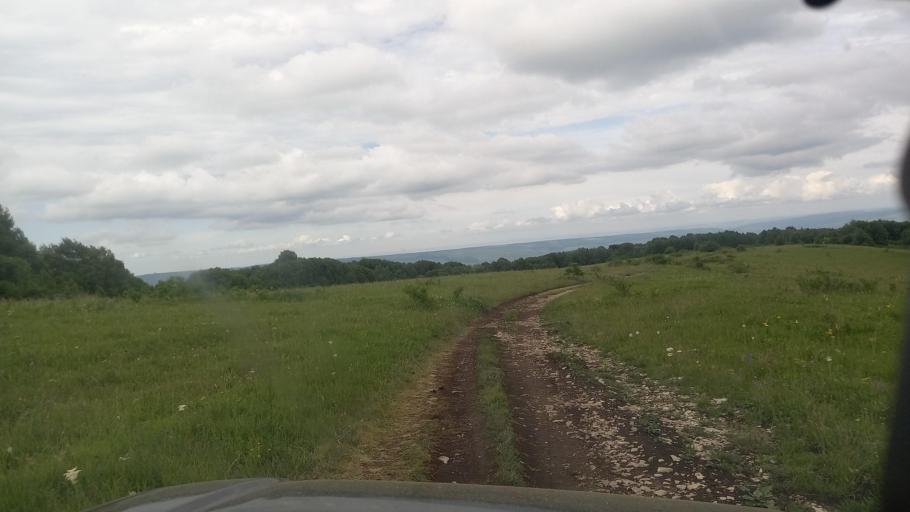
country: RU
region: Karachayevo-Cherkesiya
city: Pregradnaya
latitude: 44.0180
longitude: 41.2827
